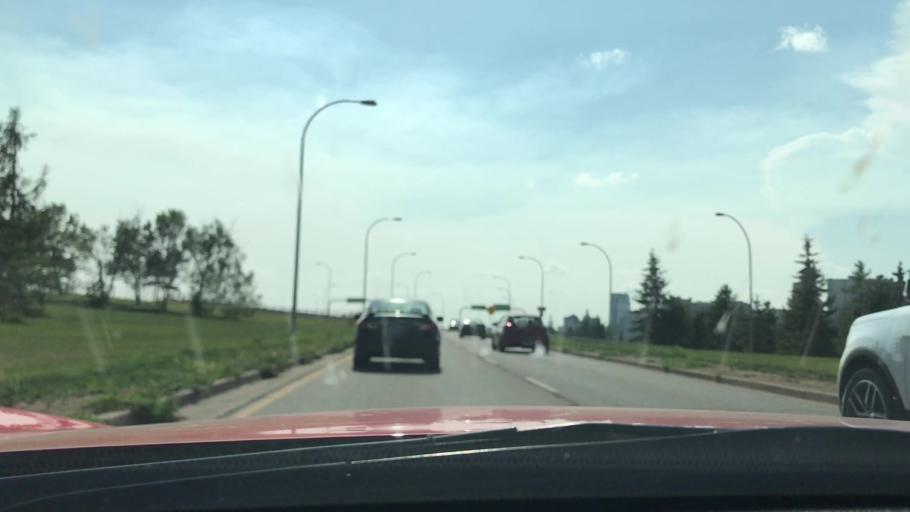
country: CA
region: Alberta
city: Edmonton
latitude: 53.5369
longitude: -113.4818
